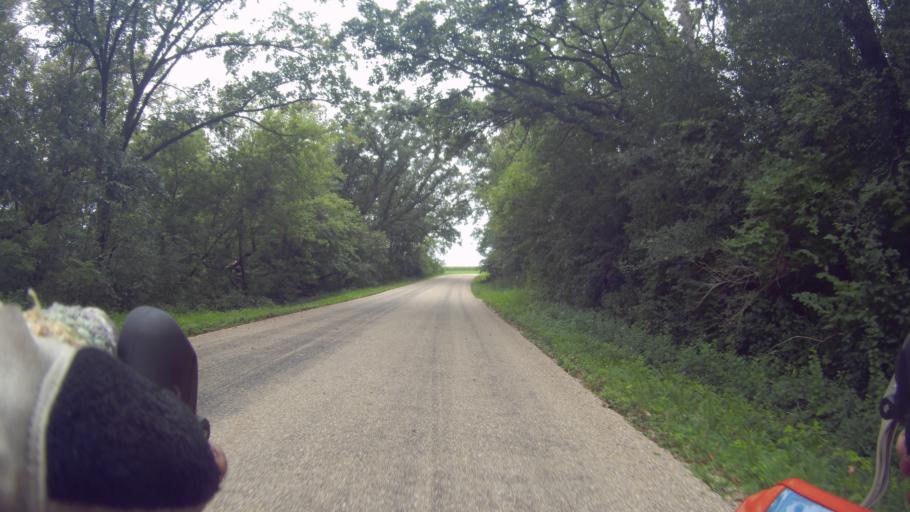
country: US
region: Wisconsin
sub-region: Dane County
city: Belleville
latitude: 42.9216
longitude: -89.5578
